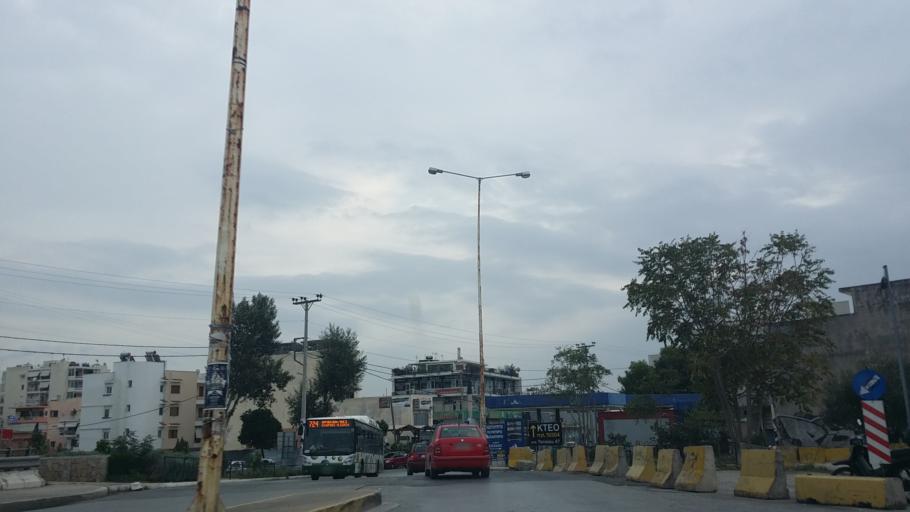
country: GR
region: Attica
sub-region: Nomarchia Athinas
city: Metamorfosi
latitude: 38.0598
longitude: 23.7561
